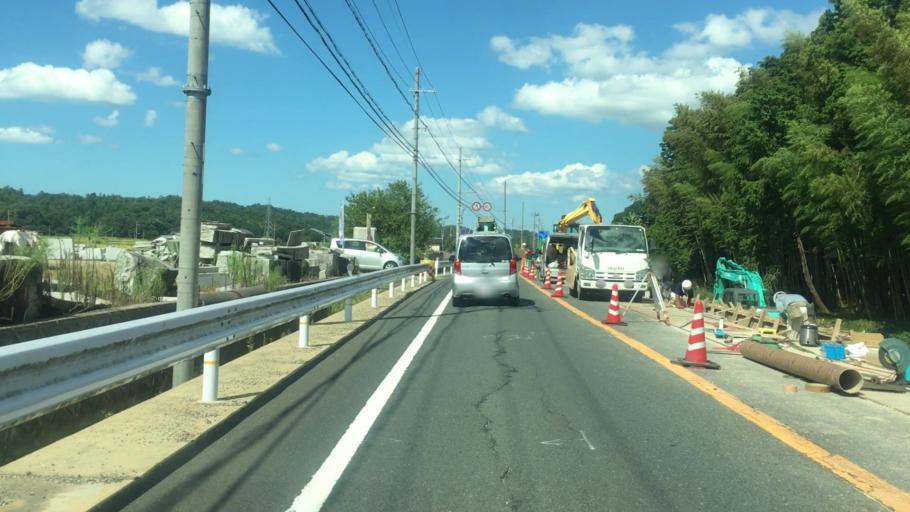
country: JP
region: Kyoto
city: Miyazu
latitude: 35.5959
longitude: 135.0439
